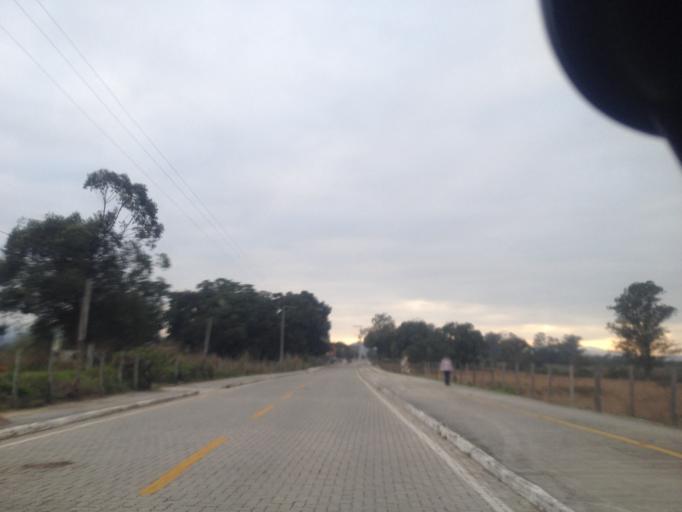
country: BR
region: Rio de Janeiro
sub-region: Porto Real
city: Porto Real
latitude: -22.4275
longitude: -44.2971
